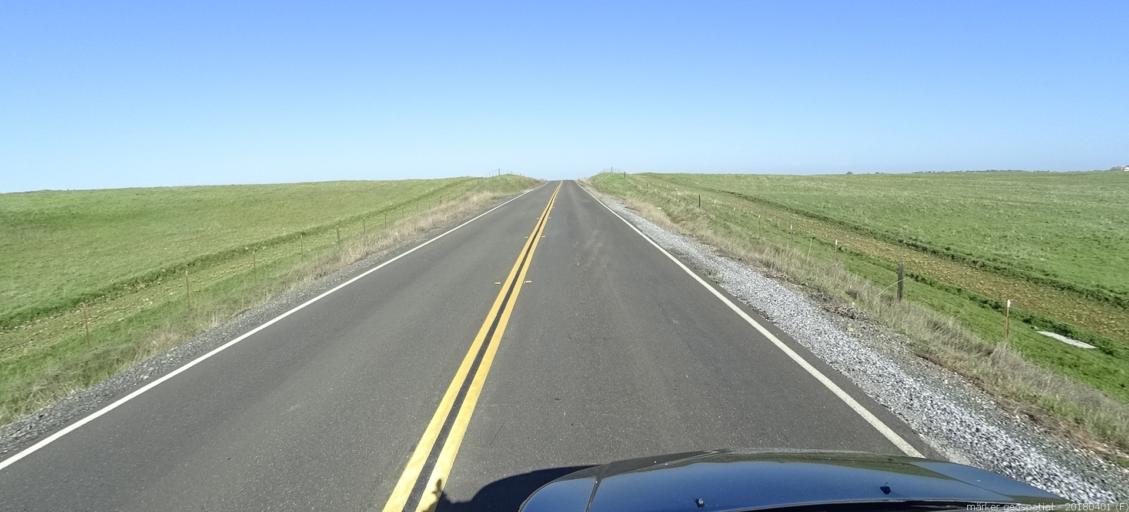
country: US
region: California
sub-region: Amador County
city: Ione
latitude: 38.4049
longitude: -121.0217
